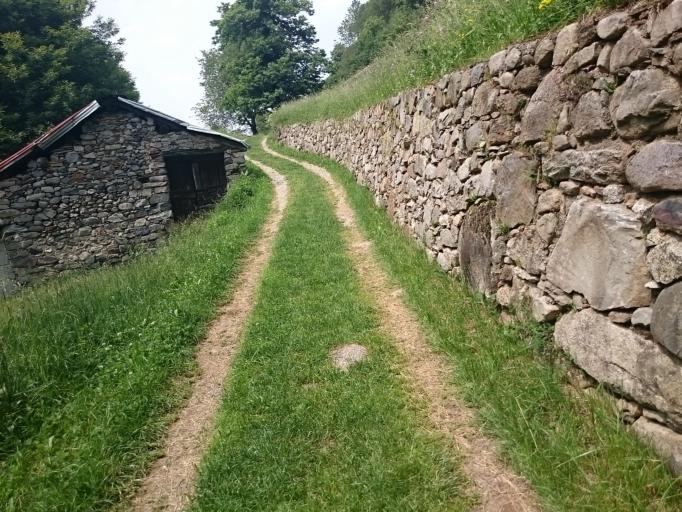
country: IT
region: Lombardy
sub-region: Provincia di Brescia
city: Paspardo
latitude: 46.0367
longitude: 10.3707
